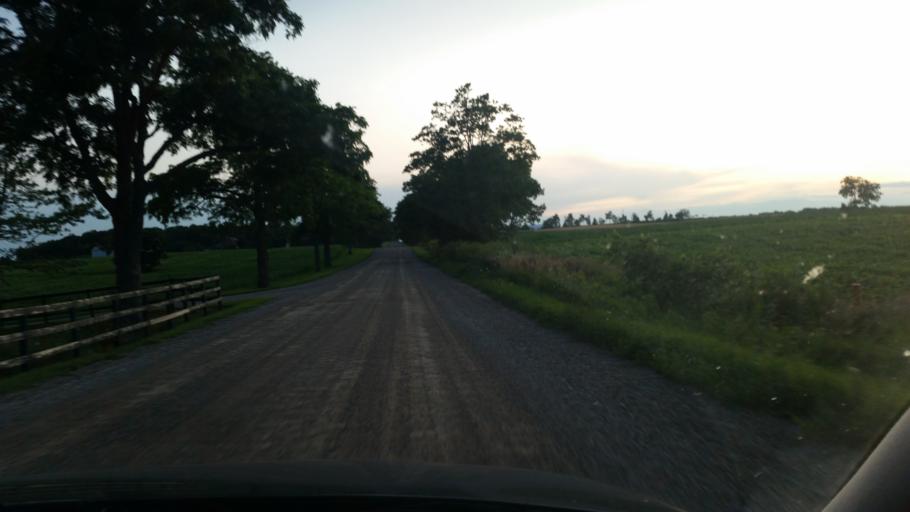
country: CA
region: Ontario
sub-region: Oxford County
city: Woodstock
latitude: 43.0368
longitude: -80.6652
